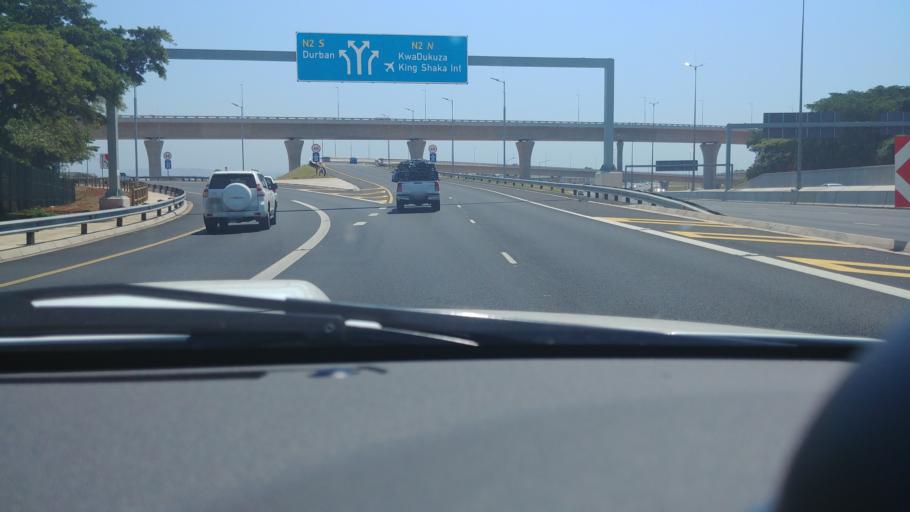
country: ZA
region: KwaZulu-Natal
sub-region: eThekwini Metropolitan Municipality
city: Durban
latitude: -29.7261
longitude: 31.0606
